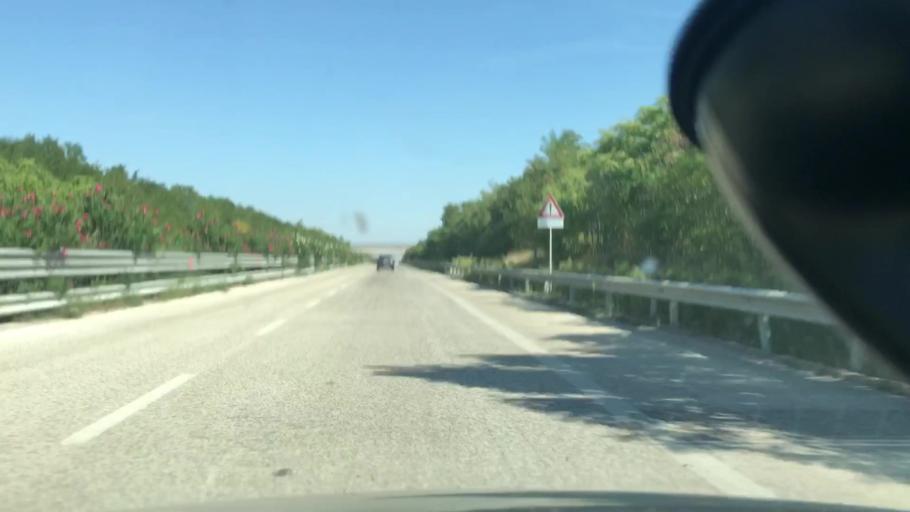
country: IT
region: Apulia
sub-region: Provincia di Foggia
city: Ordona
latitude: 41.2856
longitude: 15.5540
